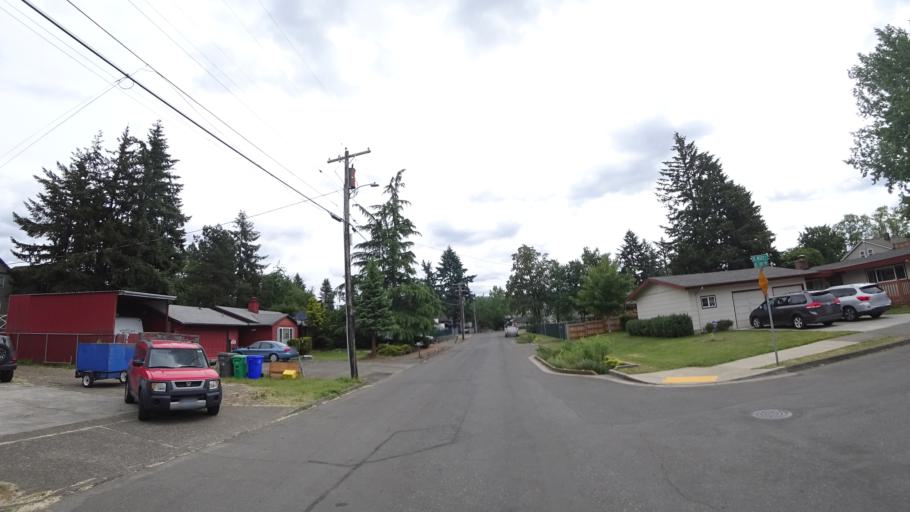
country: US
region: Oregon
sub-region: Multnomah County
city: Lents
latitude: 45.4841
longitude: -122.5420
